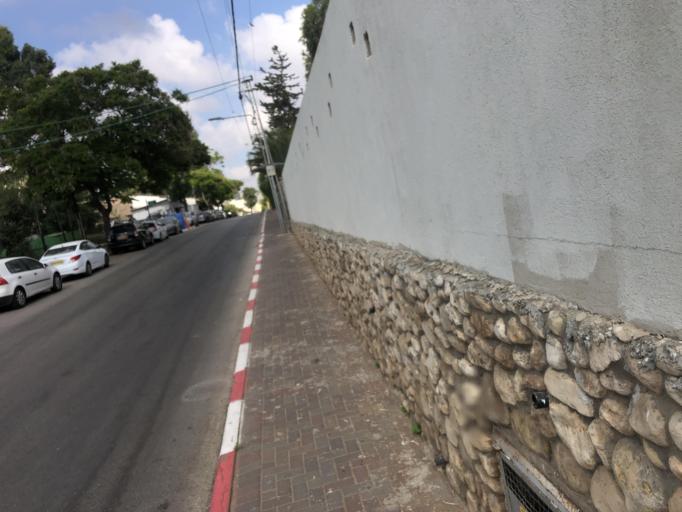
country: IL
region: Central District
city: Yehud
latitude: 32.0343
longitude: 34.8893
